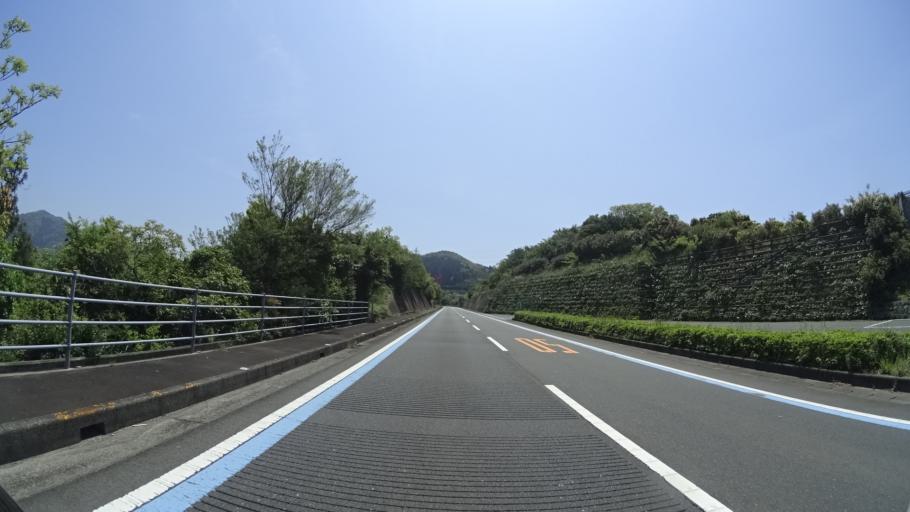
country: JP
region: Ehime
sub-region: Nishiuwa-gun
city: Ikata-cho
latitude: 33.4477
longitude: 132.2589
